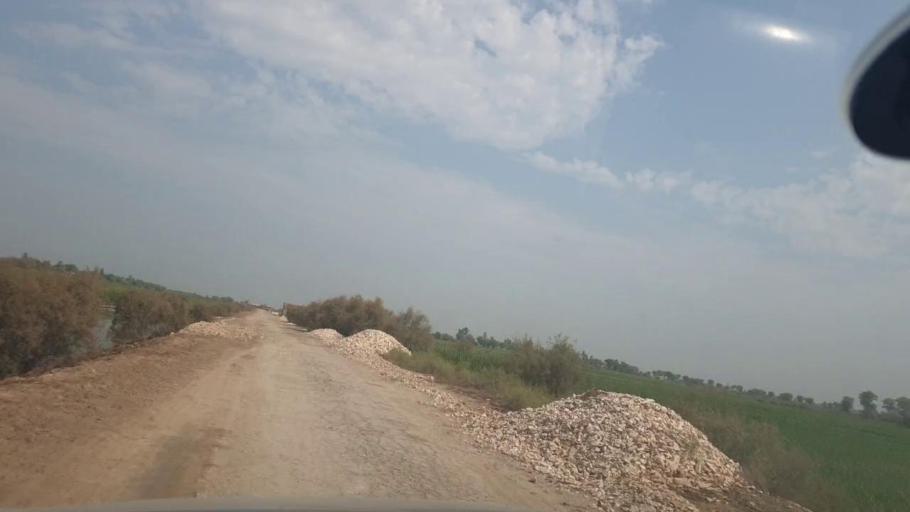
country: PK
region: Balochistan
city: Mehrabpur
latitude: 28.0987
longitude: 68.0931
